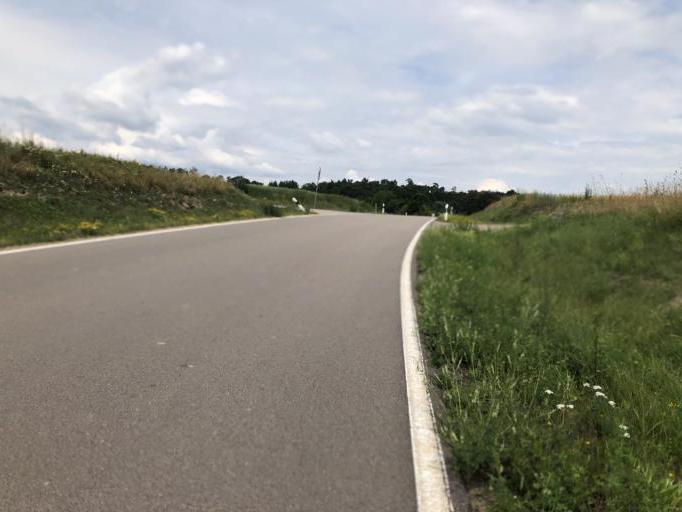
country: DE
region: Bavaria
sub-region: Regierungsbezirk Mittelfranken
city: Obermichelbach
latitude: 49.5667
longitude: 10.9290
